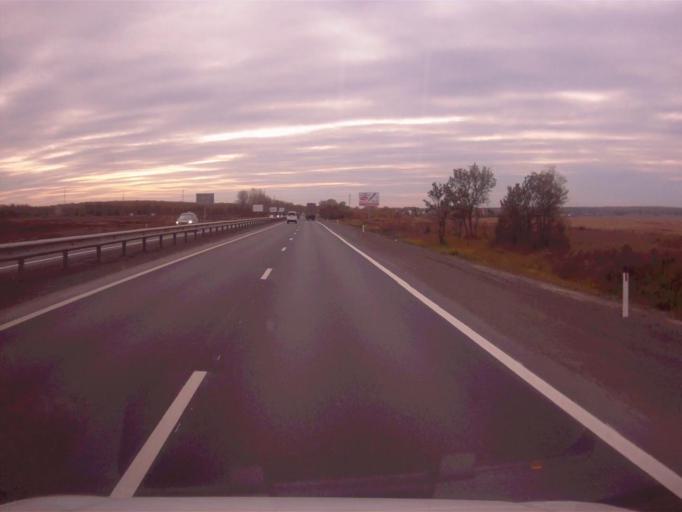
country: RU
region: Chelyabinsk
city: Roza
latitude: 54.9896
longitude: 61.4402
